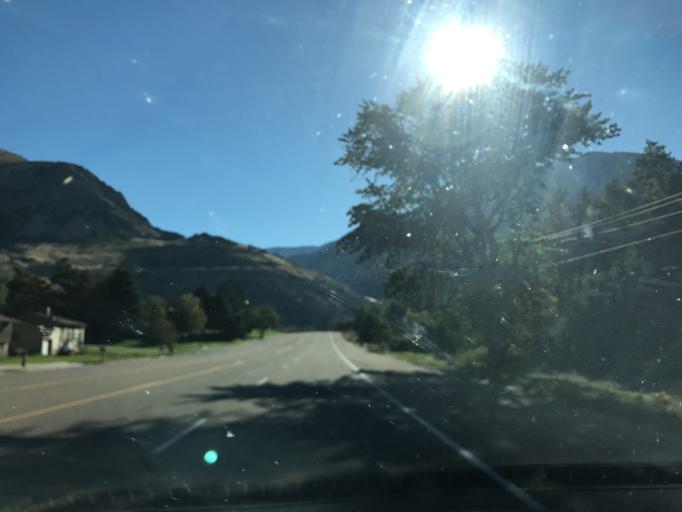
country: US
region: Utah
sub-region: Weber County
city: Ogden
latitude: 41.2401
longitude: -111.9380
